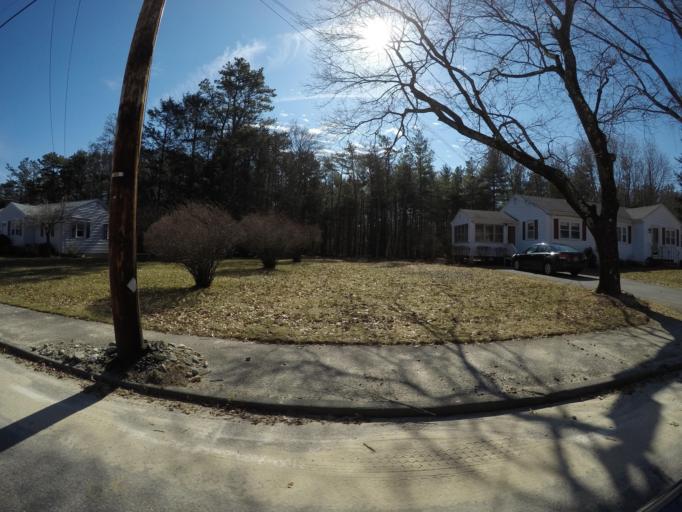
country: US
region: Massachusetts
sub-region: Norfolk County
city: Sharon
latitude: 42.1117
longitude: -71.1416
